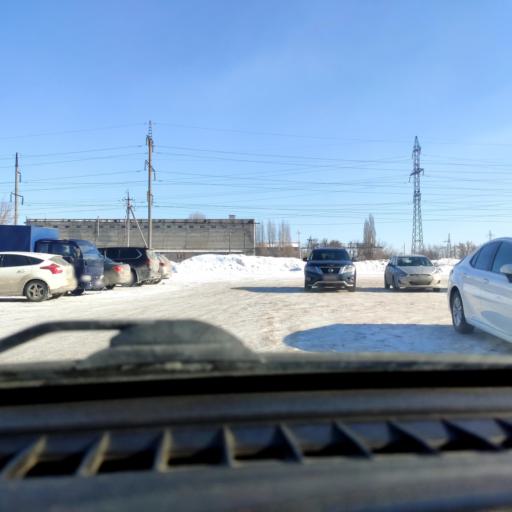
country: RU
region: Samara
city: Tol'yatti
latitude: 53.5207
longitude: 49.4650
